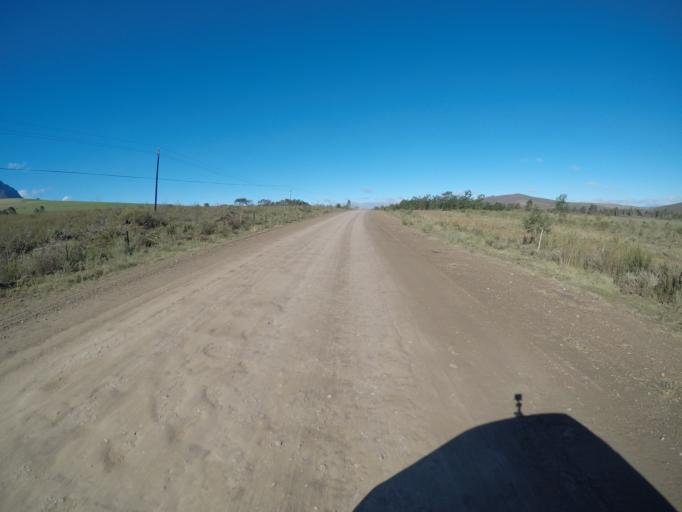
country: ZA
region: Western Cape
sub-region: Overberg District Municipality
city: Caledon
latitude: -34.0650
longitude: 19.6277
